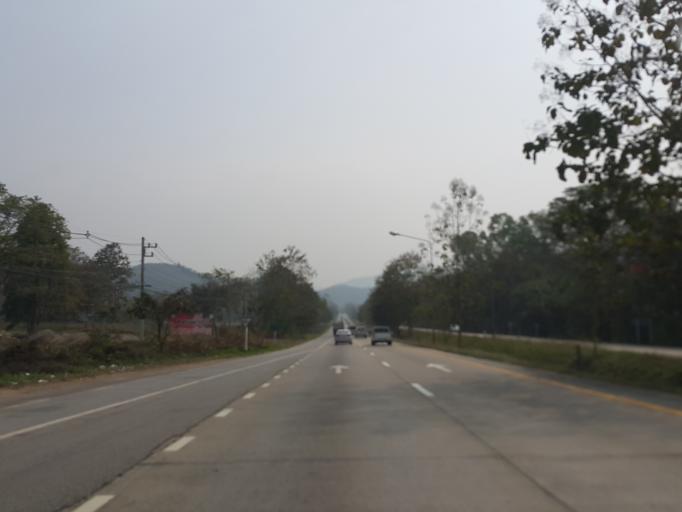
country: TH
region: Lamphun
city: Mae Tha
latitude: 18.5079
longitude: 99.1063
